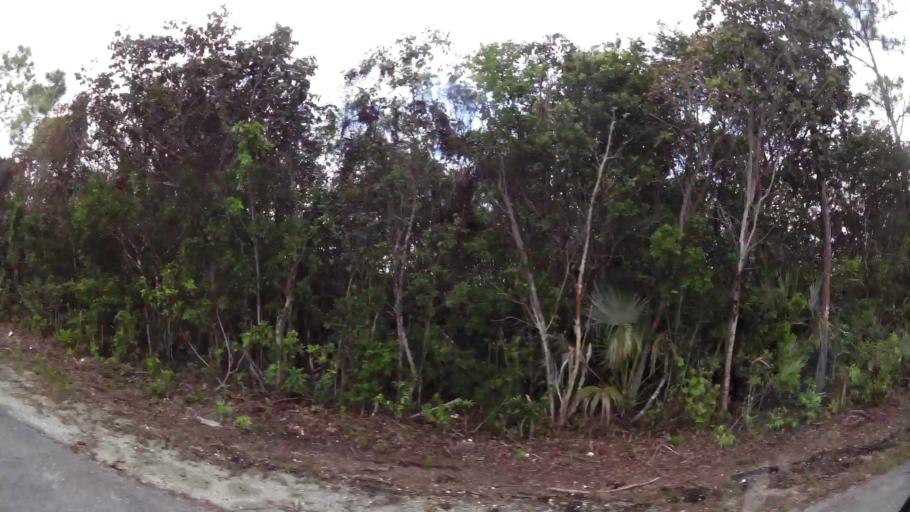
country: BS
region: Freeport
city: Lucaya
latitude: 26.5326
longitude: -78.6018
